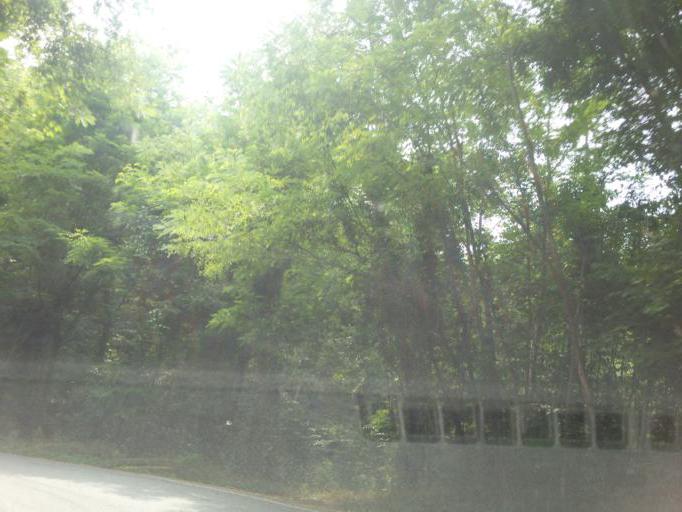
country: IT
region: Liguria
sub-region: Provincia di Genova
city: Piccarello
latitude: 44.4377
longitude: 9.0082
